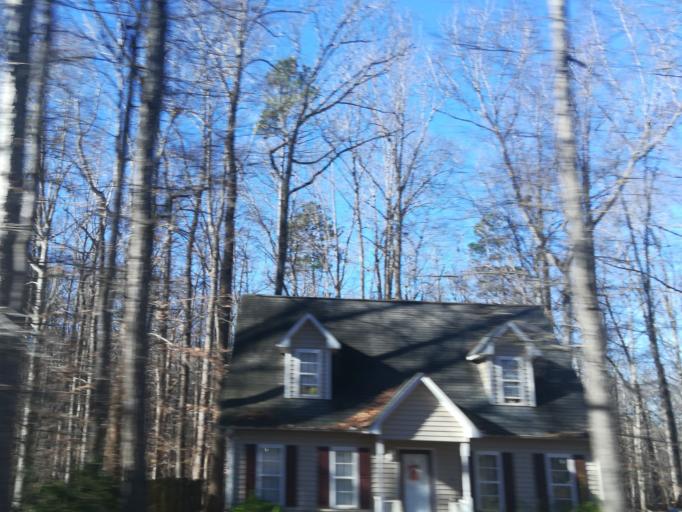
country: US
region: North Carolina
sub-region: Durham County
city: Durham
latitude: 36.0458
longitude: -78.9826
